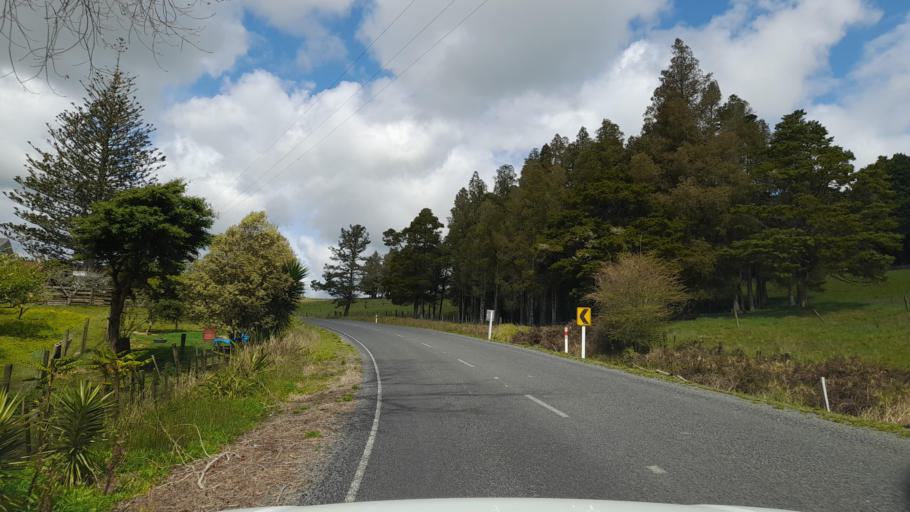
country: NZ
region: Northland
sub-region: Whangarei
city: Maungatapere
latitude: -35.6397
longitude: 174.1111
